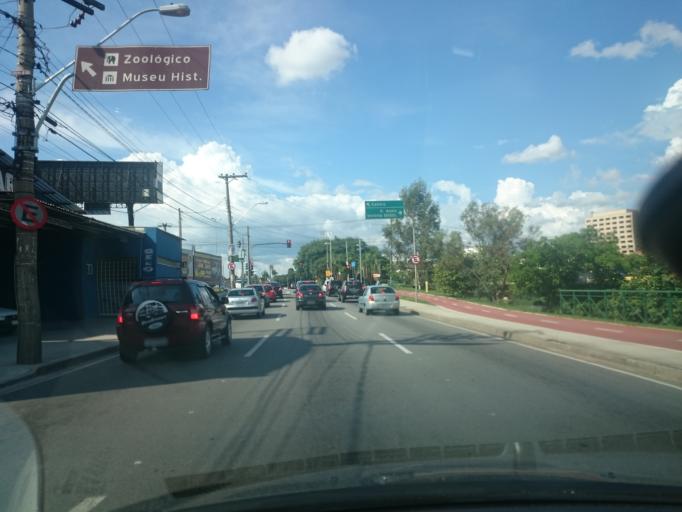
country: BR
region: Sao Paulo
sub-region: Sorocaba
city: Sorocaba
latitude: -23.5086
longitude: -47.4522
